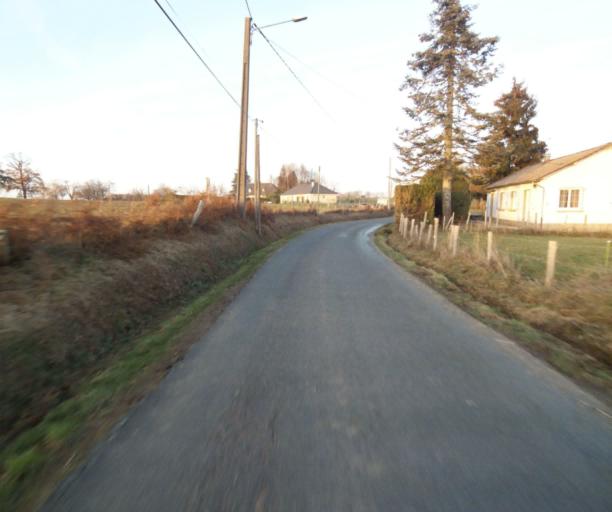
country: FR
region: Limousin
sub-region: Departement de la Correze
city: Laguenne
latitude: 45.2241
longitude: 1.8263
